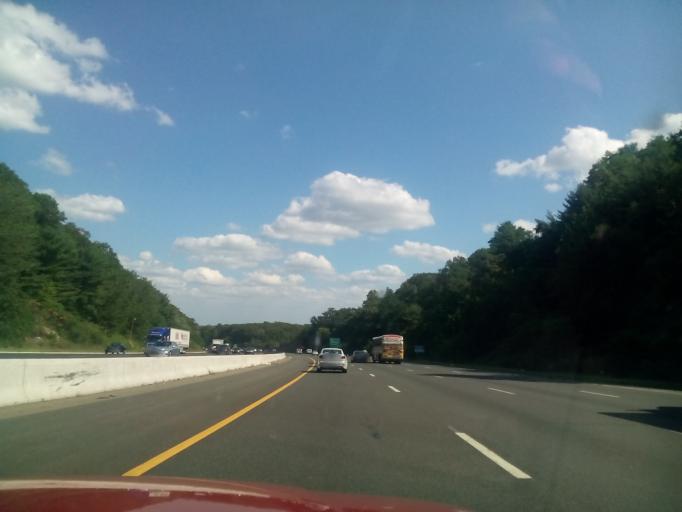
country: US
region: New Jersey
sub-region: Morris County
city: Mountain Lakes
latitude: 40.8705
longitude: -74.4615
